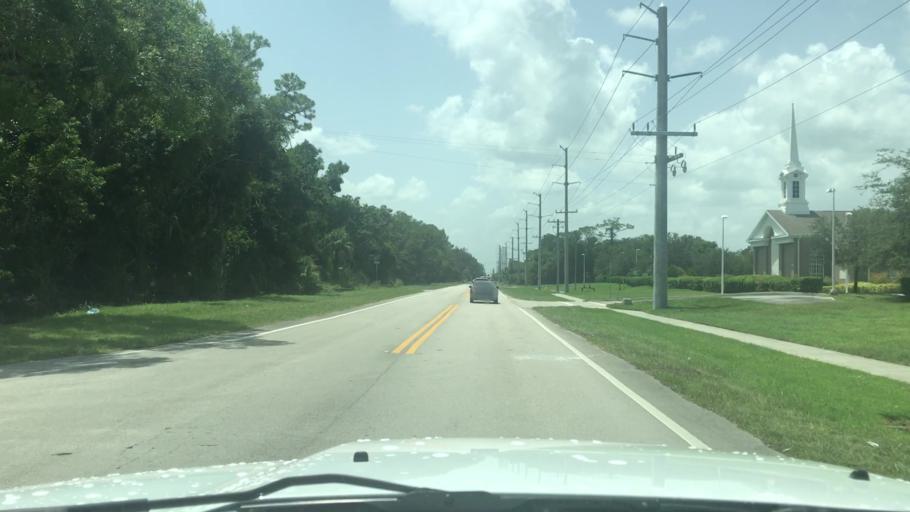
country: US
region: Florida
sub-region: Indian River County
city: Vero Beach South
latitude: 27.6238
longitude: -80.4241
